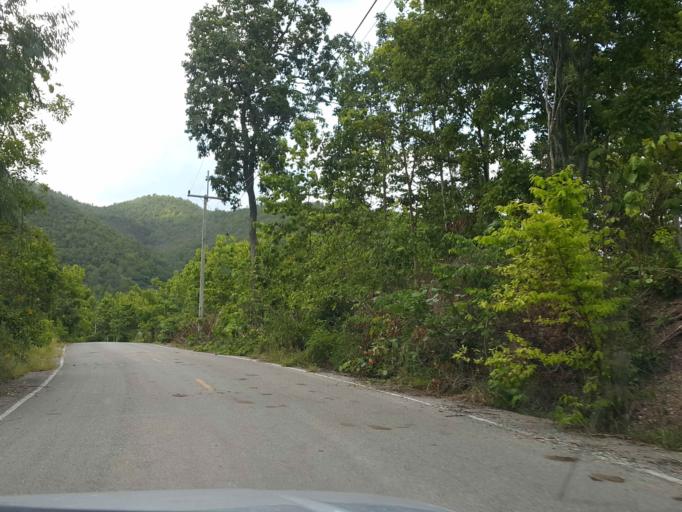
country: TH
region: Lampang
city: Thoen
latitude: 17.6529
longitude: 99.2946
